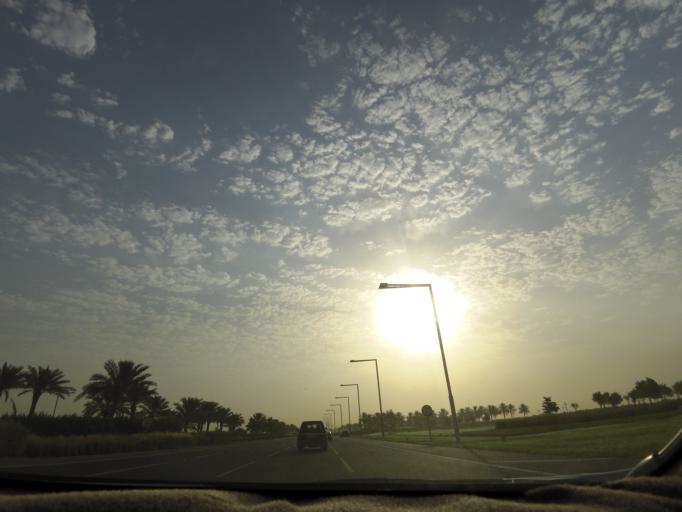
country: QA
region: Al Wakrah
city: Al Wakrah
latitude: 25.2422
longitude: 51.5957
